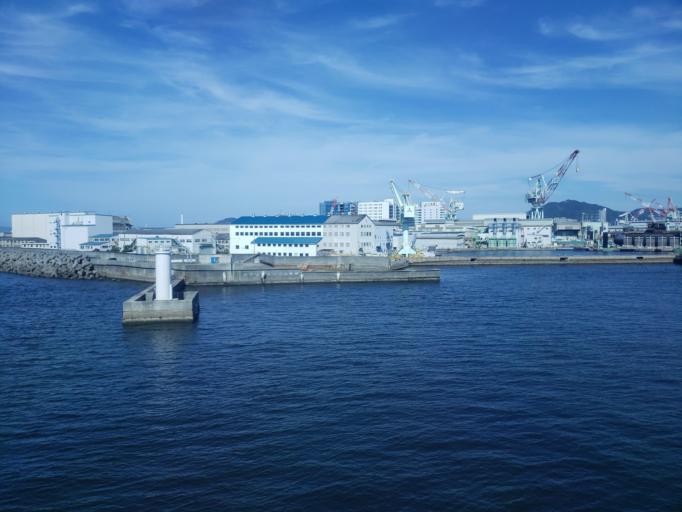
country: JP
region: Hyogo
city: Kobe
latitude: 34.6529
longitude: 135.1885
